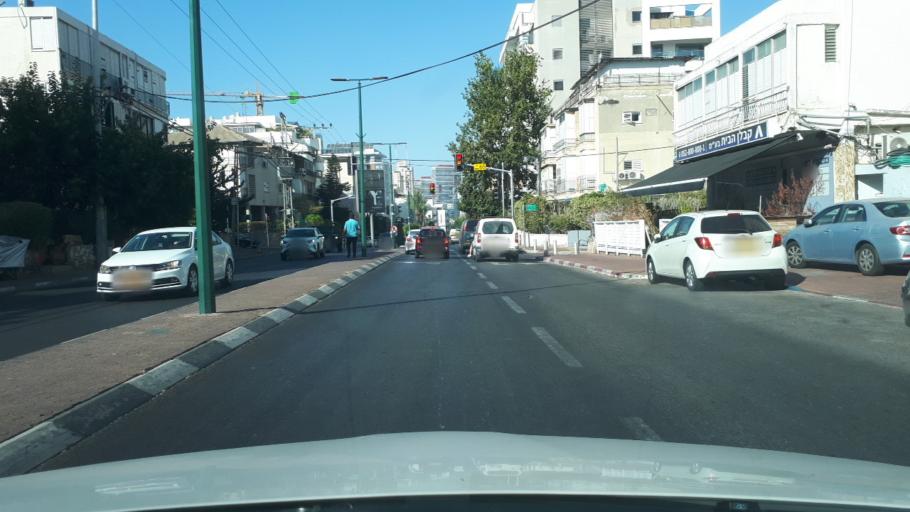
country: IL
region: Tel Aviv
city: Ramat Gan
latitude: 32.0797
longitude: 34.8198
